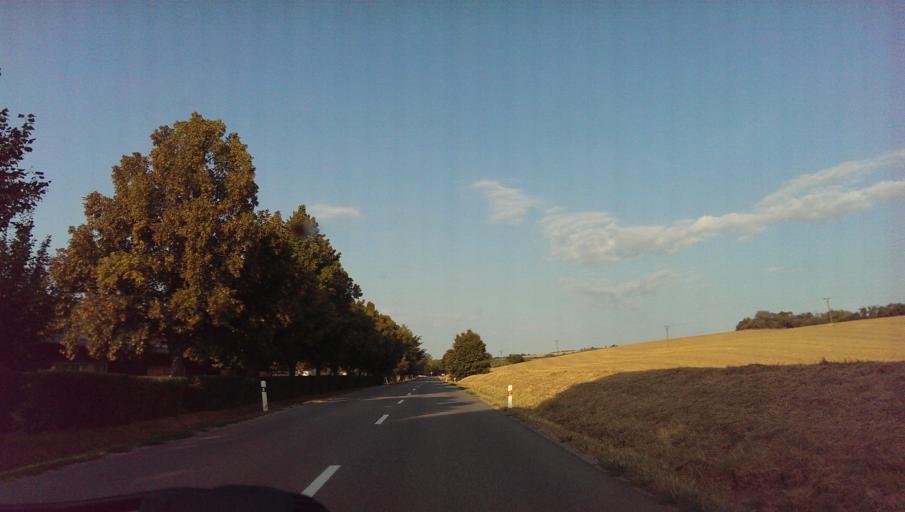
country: CZ
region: Zlin
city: Borsice
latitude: 49.0625
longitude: 17.3383
